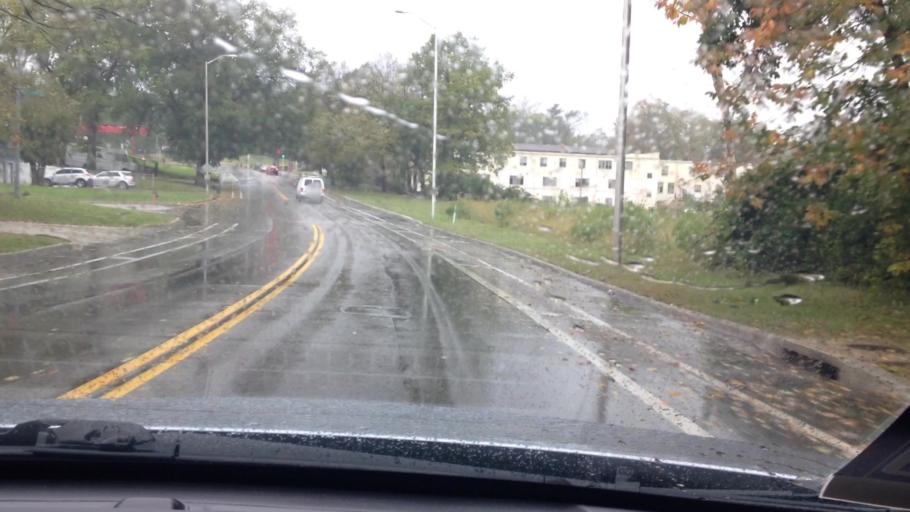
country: US
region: Missouri
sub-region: Jackson County
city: Raytown
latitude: 38.9982
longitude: -94.5405
